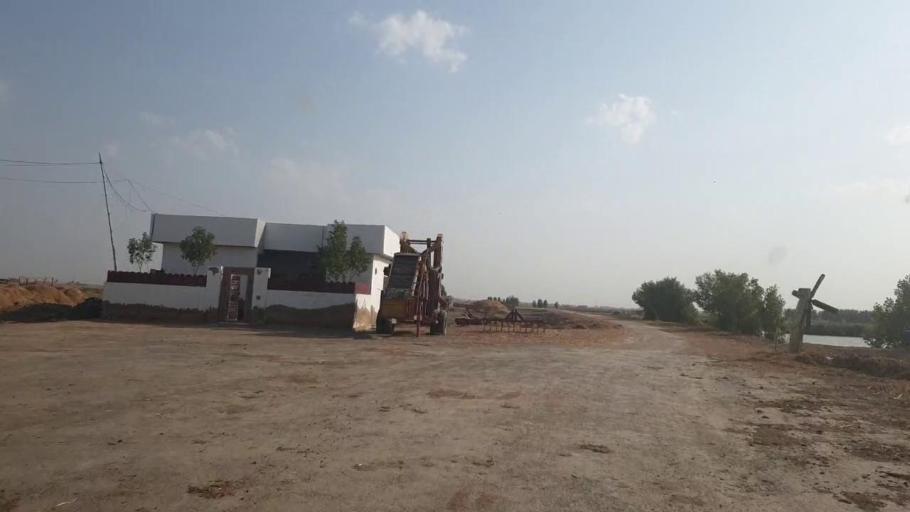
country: PK
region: Sindh
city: Kario
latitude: 24.5795
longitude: 68.5418
